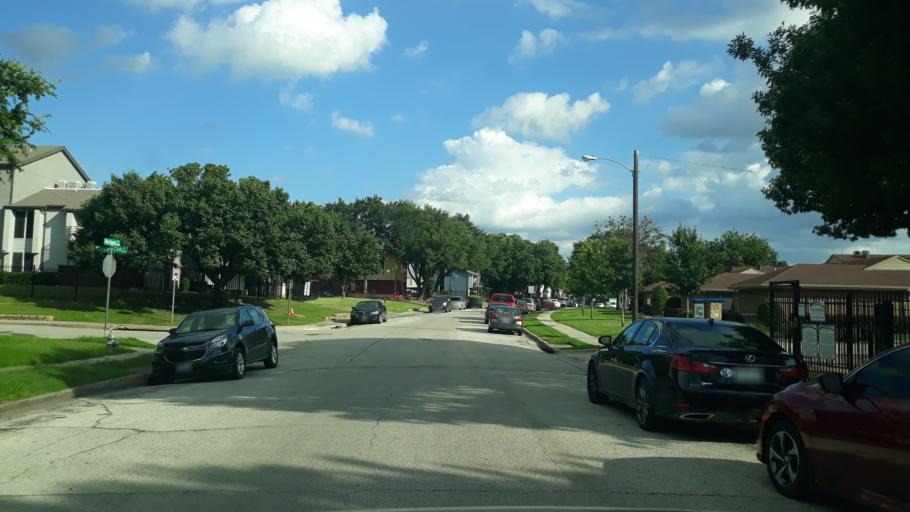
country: US
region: Texas
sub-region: Dallas County
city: Irving
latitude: 32.8599
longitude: -97.0053
